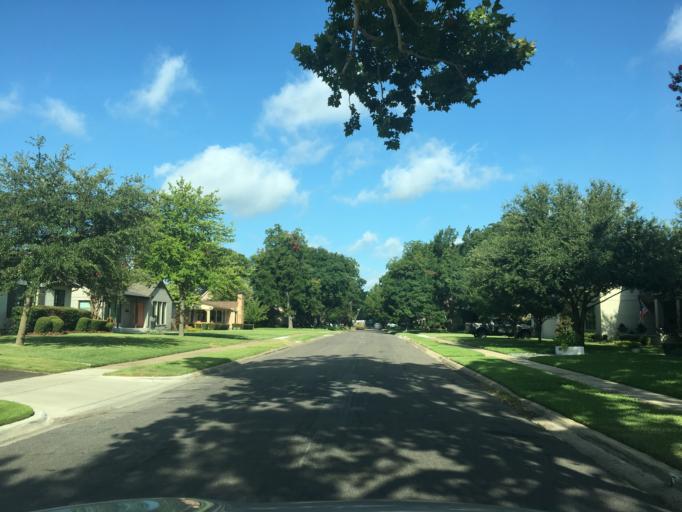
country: US
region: Texas
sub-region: Dallas County
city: Highland Park
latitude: 32.8334
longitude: -96.7482
